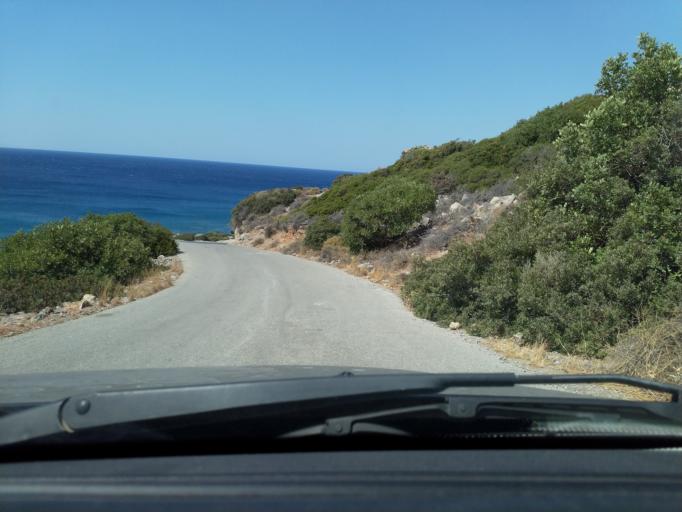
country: GR
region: Crete
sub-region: Nomos Rethymnis
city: Agia Foteini
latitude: 35.1391
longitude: 24.5291
